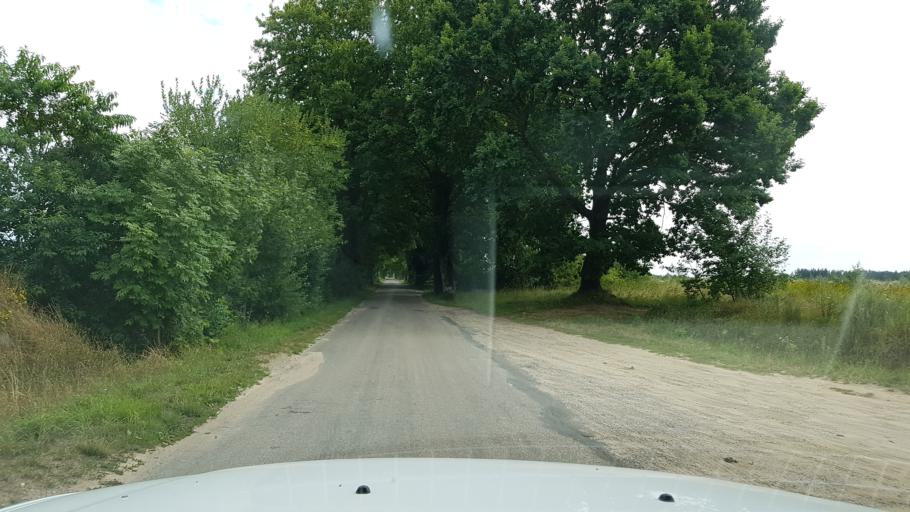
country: PL
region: West Pomeranian Voivodeship
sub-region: Powiat koszalinski
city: Mielno
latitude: 54.1660
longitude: 16.0595
